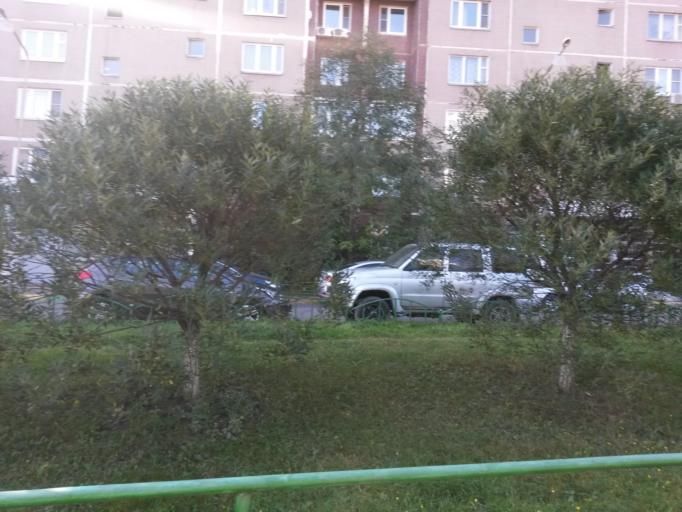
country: RU
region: Moscow
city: Mar'ino
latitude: 55.6467
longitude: 37.7396
